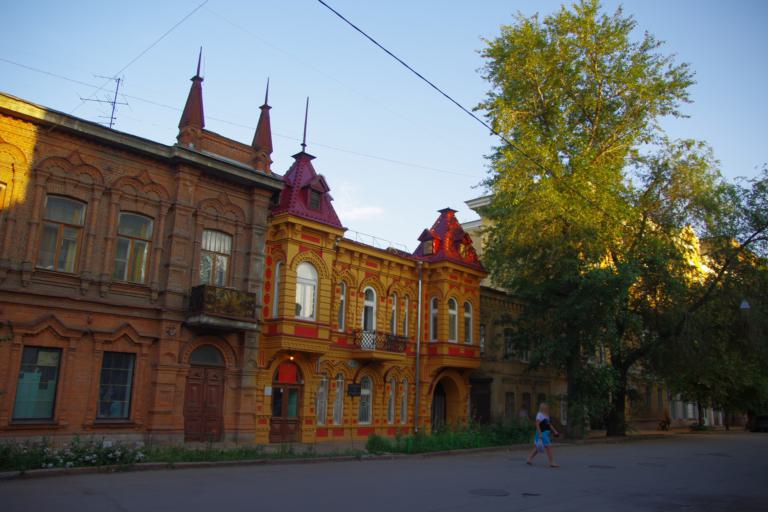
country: RU
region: Samara
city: Samara
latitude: 53.1925
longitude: 50.1003
